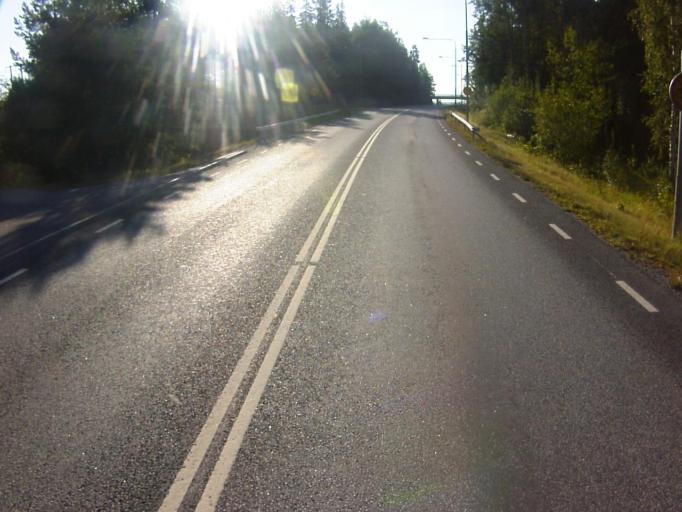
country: SE
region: Soedermanland
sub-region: Eskilstuna Kommun
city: Hallbybrunn
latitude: 59.3973
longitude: 16.4366
